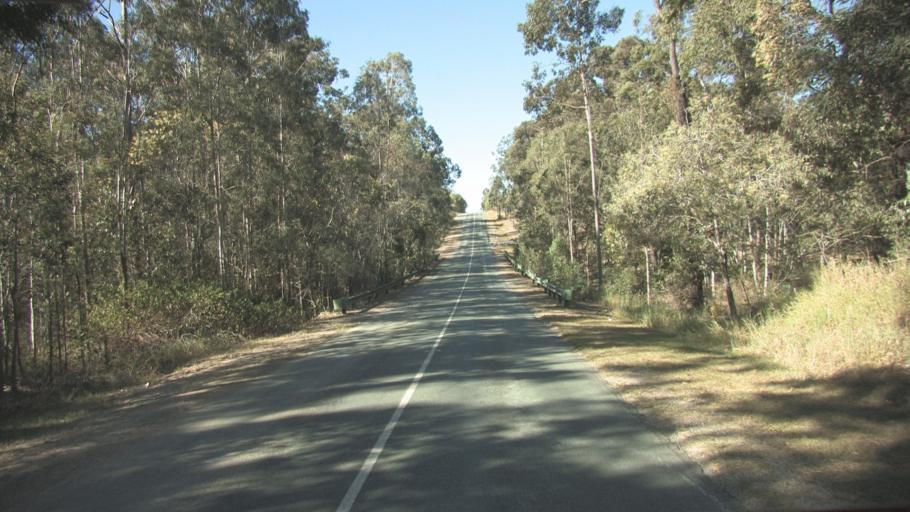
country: AU
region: Queensland
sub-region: Ipswich
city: Springfield Lakes
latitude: -27.7307
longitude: 152.9323
